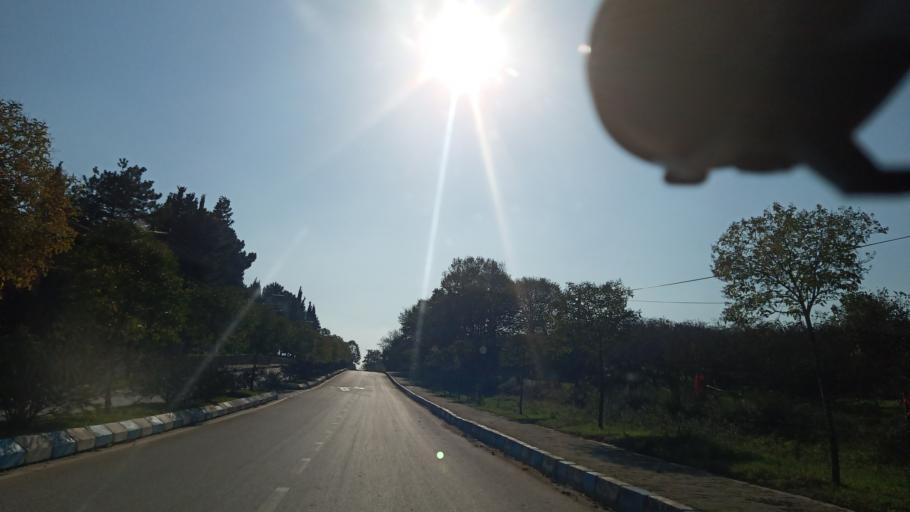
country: TR
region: Sakarya
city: Karasu
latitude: 41.0676
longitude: 30.8030
